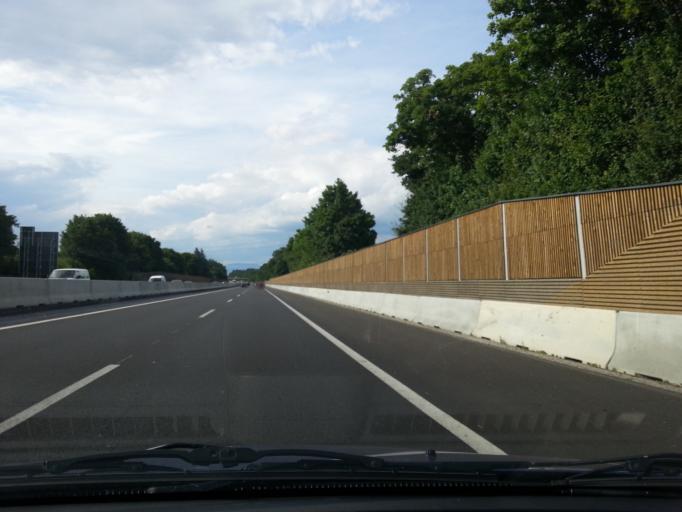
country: AT
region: Styria
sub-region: Politischer Bezirk Leibnitz
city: Weitendorf
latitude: 46.9029
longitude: 15.4724
